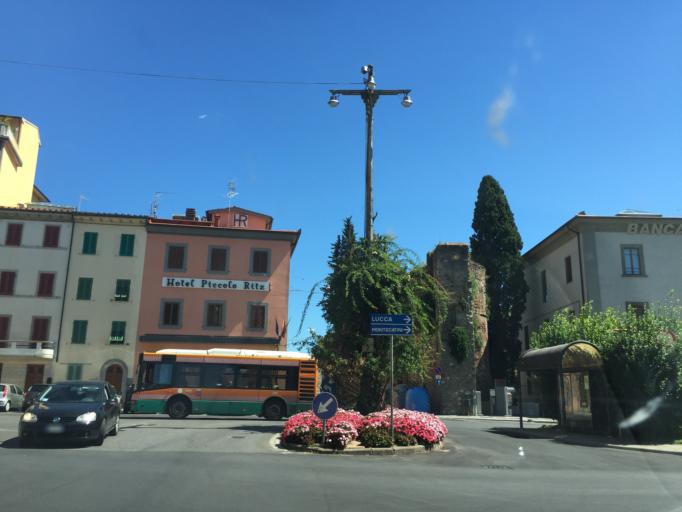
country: IT
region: Tuscany
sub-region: Provincia di Pistoia
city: Pistoia
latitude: 43.9294
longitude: 10.9145
